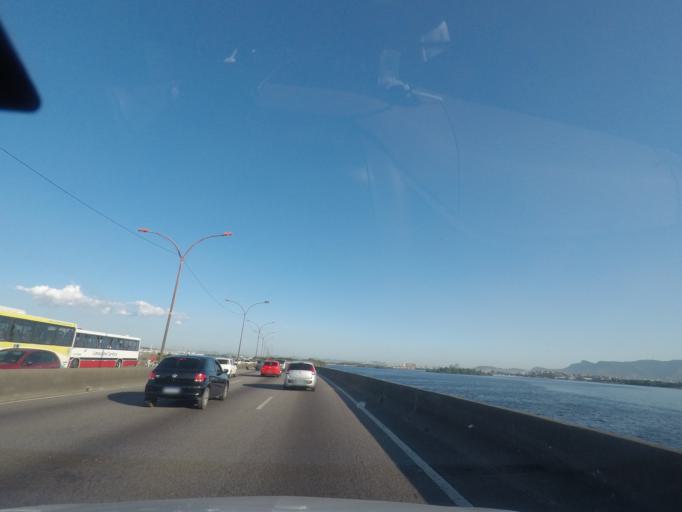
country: BR
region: Rio de Janeiro
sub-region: Duque De Caxias
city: Duque de Caxias
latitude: -22.8142
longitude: -43.2680
